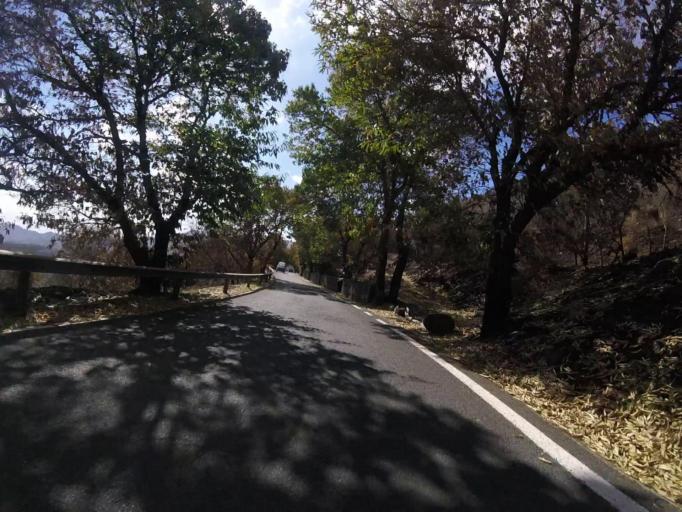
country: ES
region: Canary Islands
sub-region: Provincia de Las Palmas
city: Valleseco
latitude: 28.0117
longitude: -15.5852
